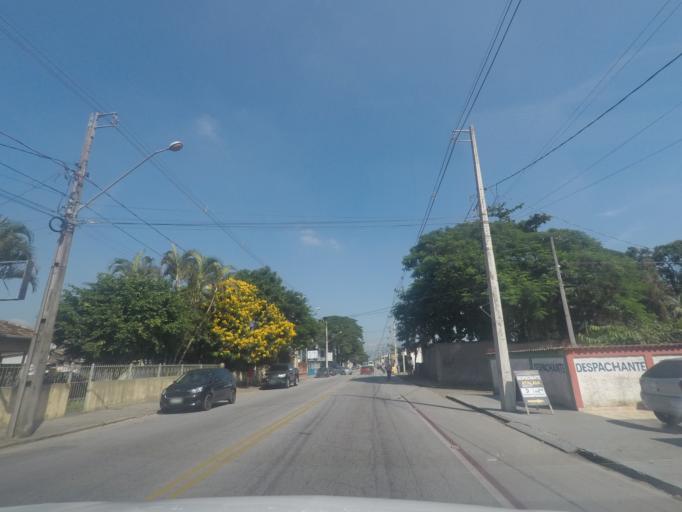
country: BR
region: Parana
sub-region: Paranagua
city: Paranagua
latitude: -25.5321
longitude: -48.5233
